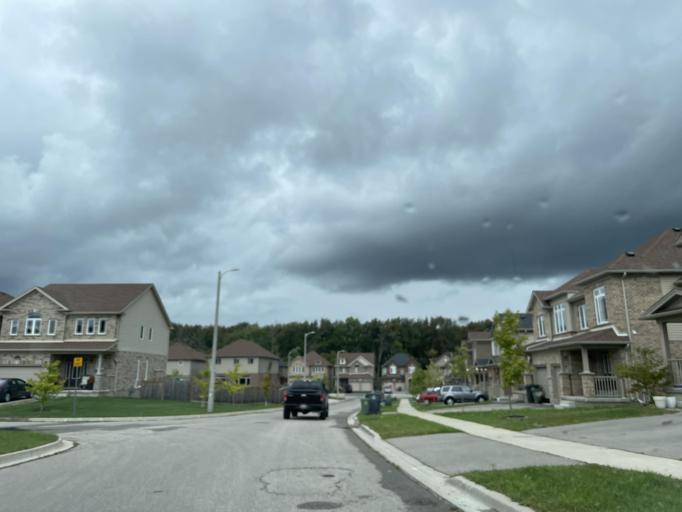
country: CA
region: Ontario
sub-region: Wellington County
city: Guelph
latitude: 43.5220
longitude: -80.3070
